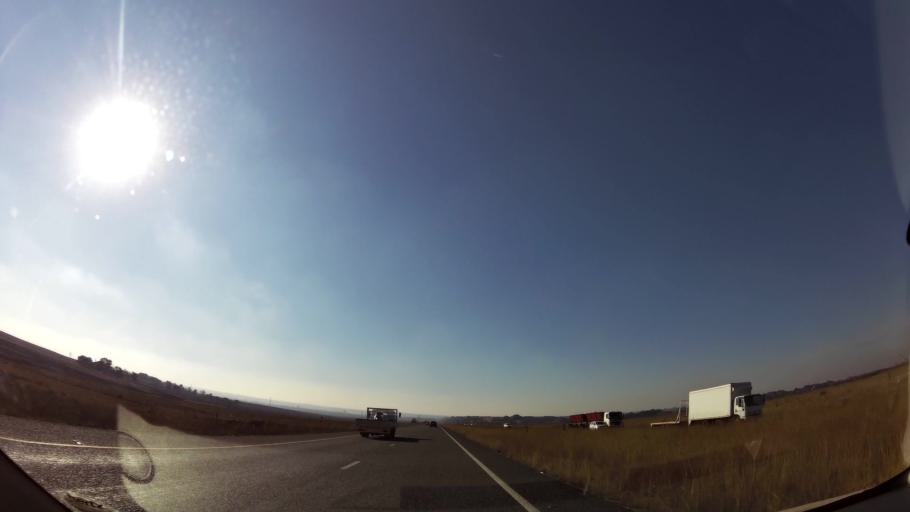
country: ZA
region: Mpumalanga
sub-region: Nkangala District Municipality
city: Witbank
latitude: -26.0196
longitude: 28.9996
